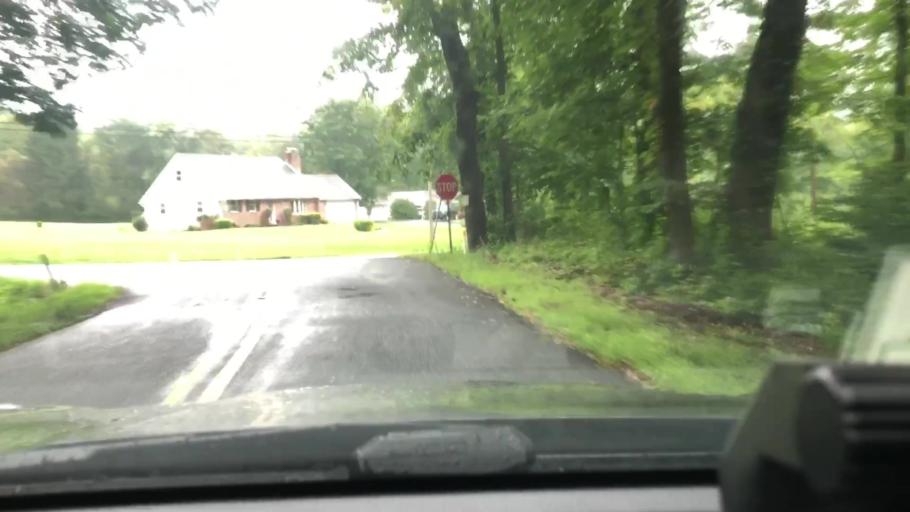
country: US
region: Pennsylvania
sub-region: Lehigh County
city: Macungie
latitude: 40.4740
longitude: -75.5480
